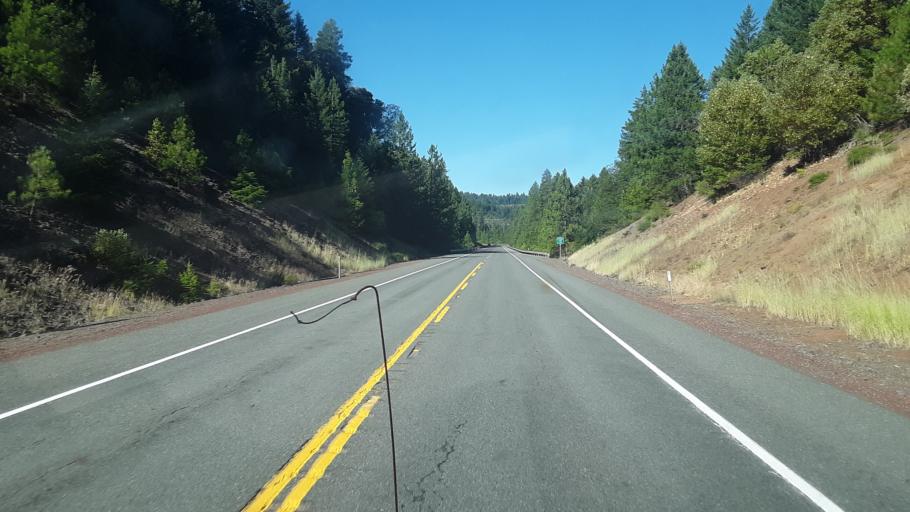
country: US
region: Oregon
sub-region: Jackson County
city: Shady Cove
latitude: 42.6726
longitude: -122.6359
